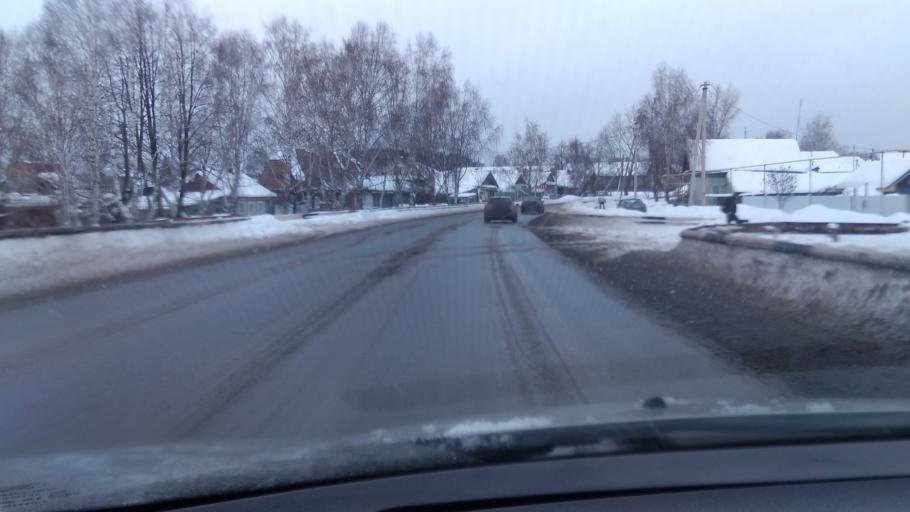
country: RU
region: Sverdlovsk
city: Nikolo-Pavlovskoye
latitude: 57.7857
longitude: 60.0558
